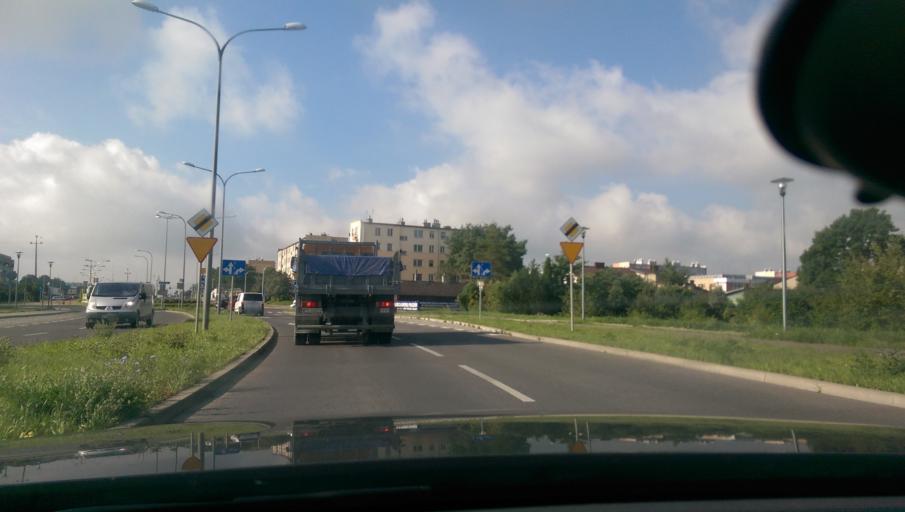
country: PL
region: Masovian Voivodeship
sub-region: Powiat ciechanowski
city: Ciechanow
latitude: 52.8825
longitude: 20.6283
